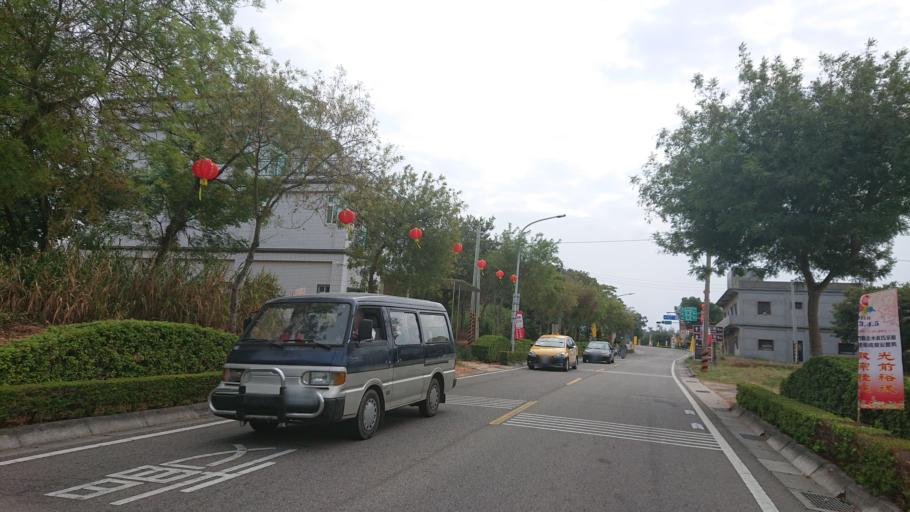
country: TW
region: Fukien
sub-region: Kinmen
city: Jincheng
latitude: 24.4116
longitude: 118.2986
